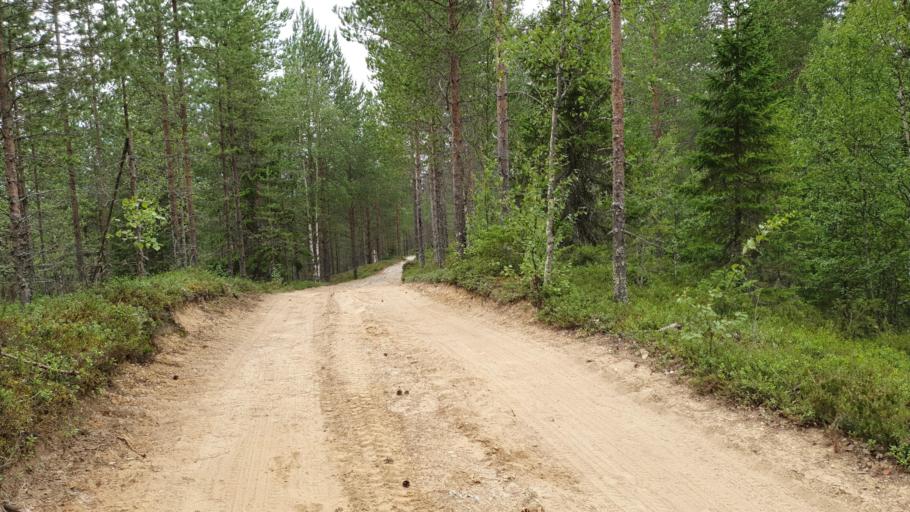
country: RU
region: Republic of Karelia
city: Kostomuksha
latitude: 64.7548
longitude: 29.9376
